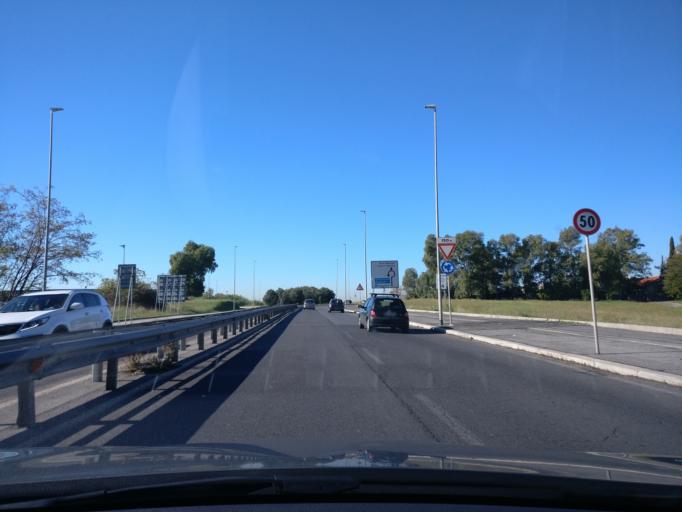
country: IT
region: Latium
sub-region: Citta metropolitana di Roma Capitale
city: Frascati
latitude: 41.8569
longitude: 12.6232
